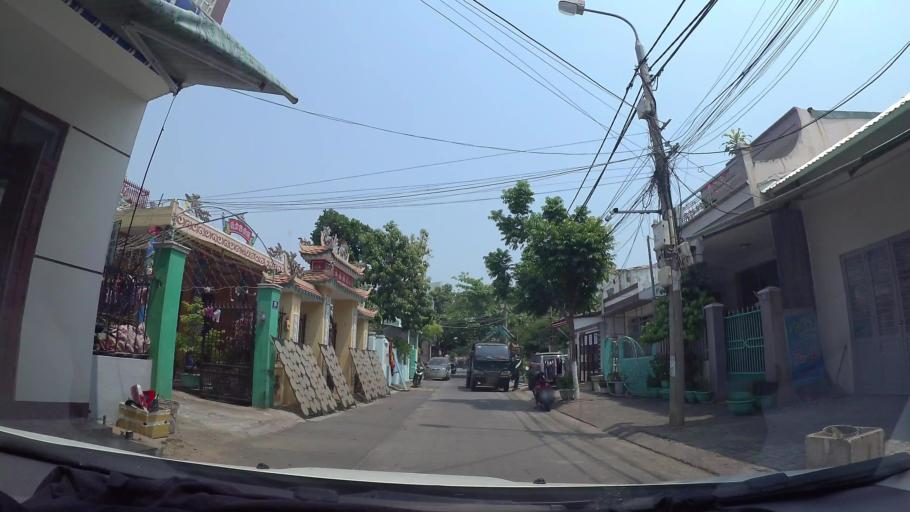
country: VN
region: Da Nang
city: Cam Le
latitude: 16.0171
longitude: 108.2064
